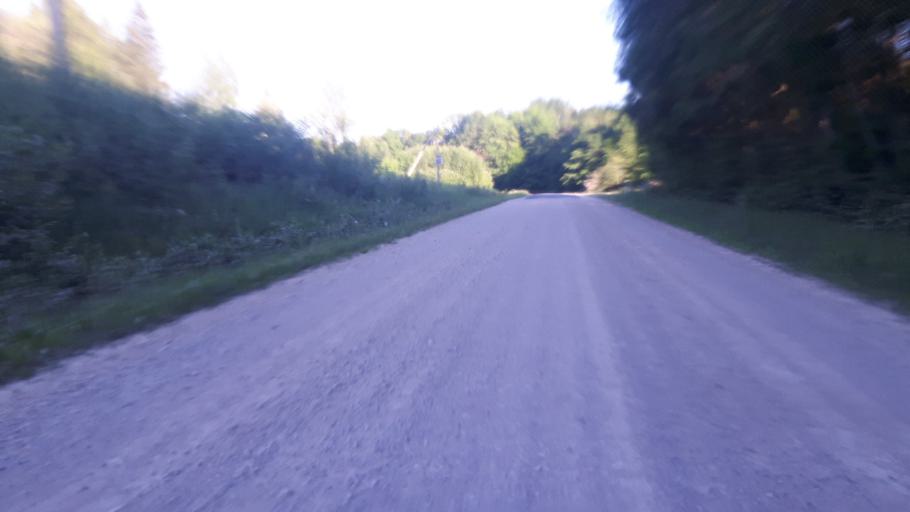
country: EE
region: Raplamaa
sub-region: Jaervakandi vald
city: Jarvakandi
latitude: 58.8128
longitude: 24.9159
